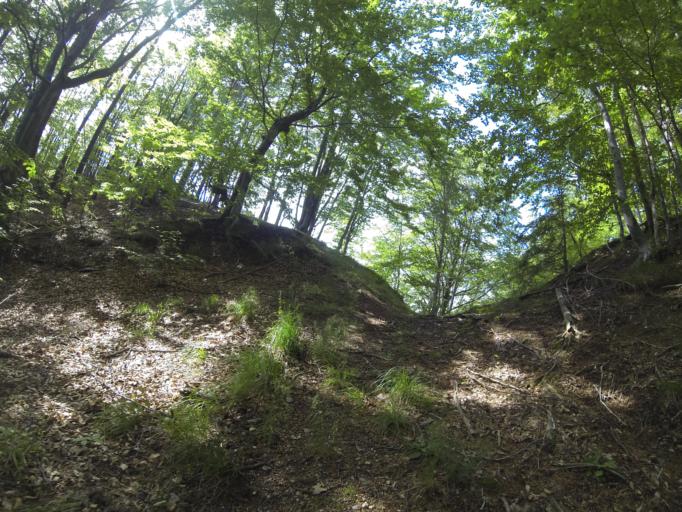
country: RO
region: Valcea
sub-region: Comuna Barbatesti
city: Barbatesti
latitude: 45.2525
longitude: 24.1575
